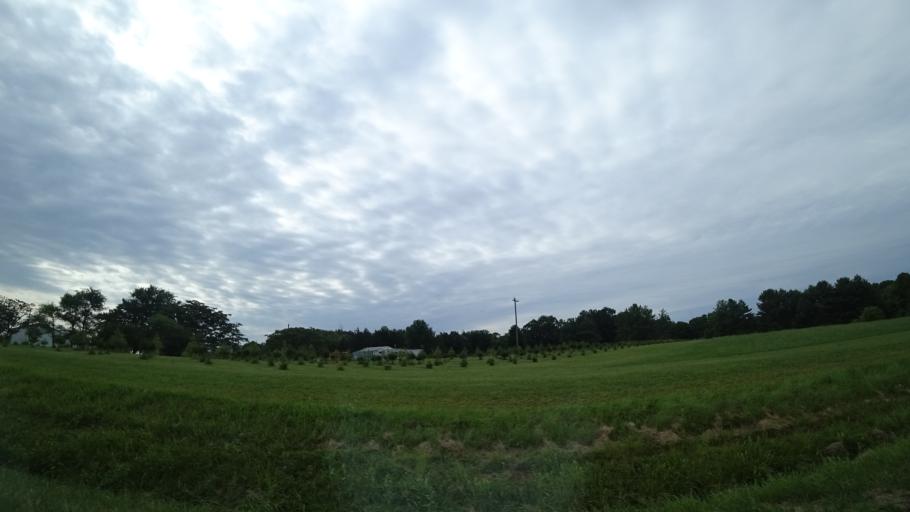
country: US
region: Virginia
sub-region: Spotsylvania County
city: Spotsylvania
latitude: 38.1466
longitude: -77.7158
